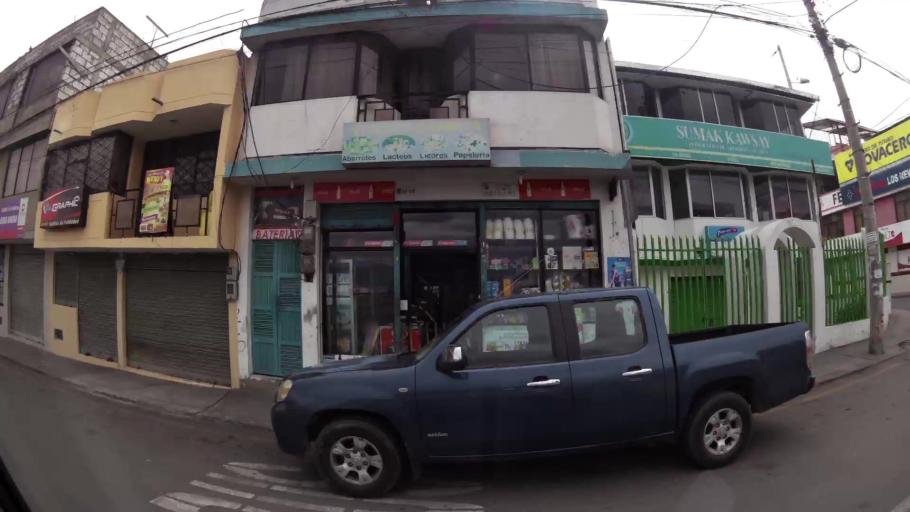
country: EC
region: Cotopaxi
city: Latacunga
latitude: -0.9341
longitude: -78.6219
